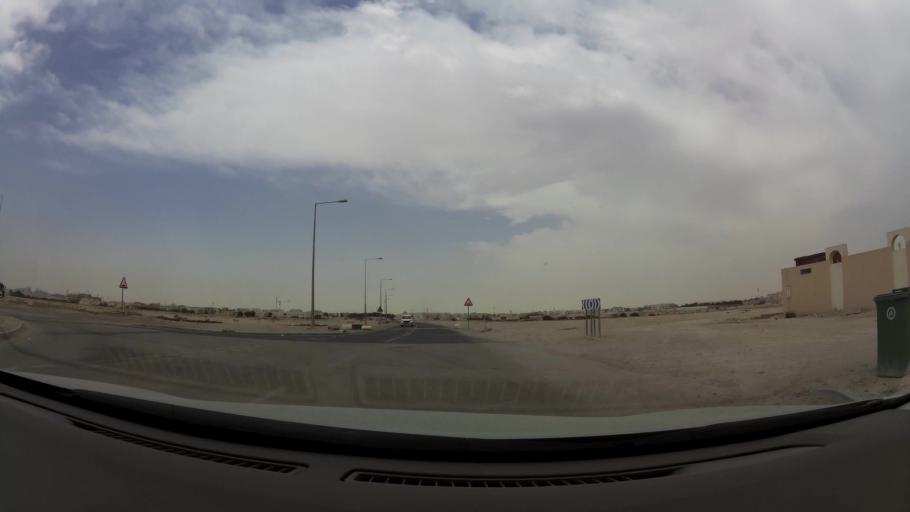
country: QA
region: Baladiyat ar Rayyan
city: Ar Rayyan
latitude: 25.2832
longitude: 51.4567
